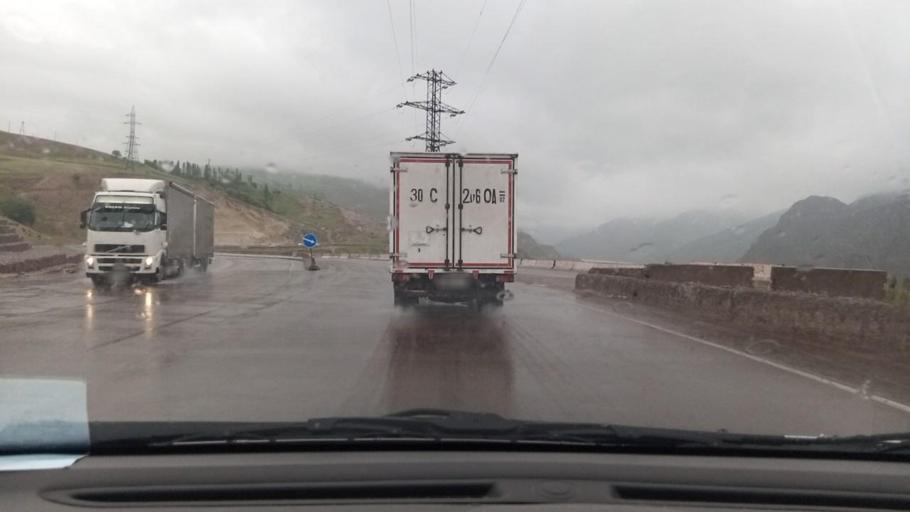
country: UZ
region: Toshkent
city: Angren
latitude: 41.0692
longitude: 70.2412
